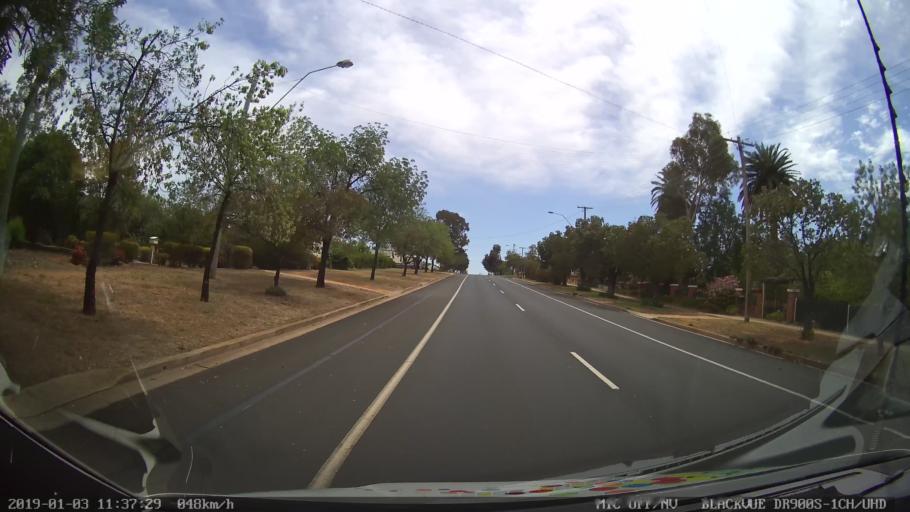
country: AU
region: New South Wales
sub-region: Weddin
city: Grenfell
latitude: -33.9026
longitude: 148.1613
